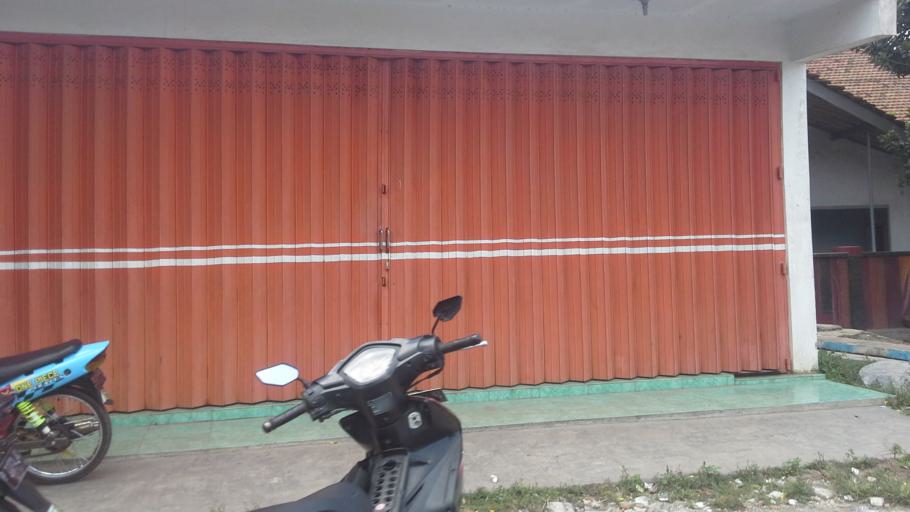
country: ID
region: East Java
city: Bondowoso
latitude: -7.9092
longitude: 113.8519
